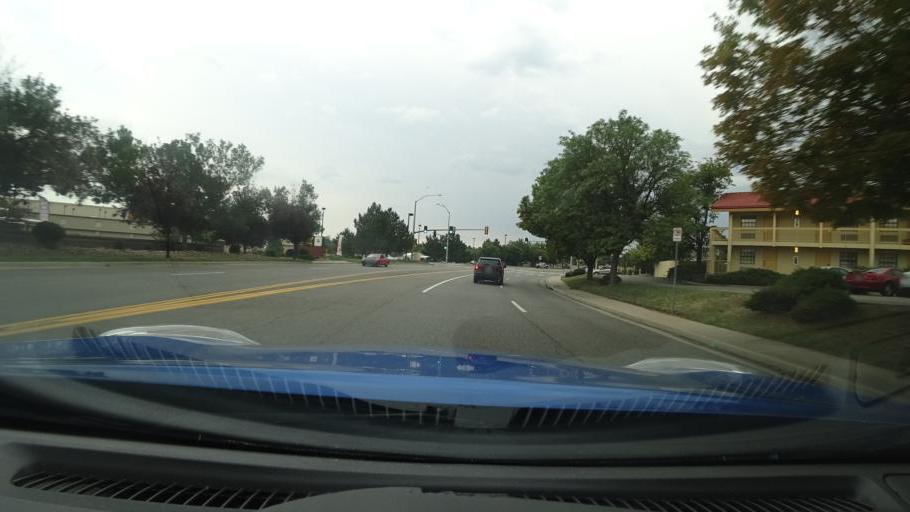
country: US
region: Colorado
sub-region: Adams County
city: Aurora
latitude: 39.6986
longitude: -104.8268
